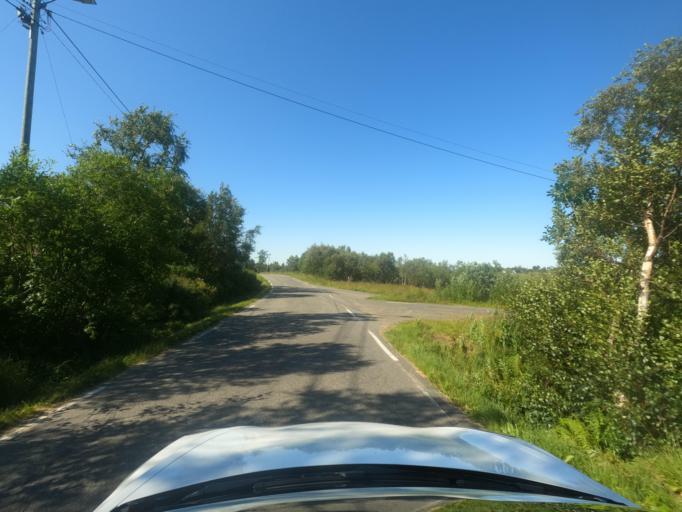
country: NO
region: Nordland
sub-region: Hadsel
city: Melbu
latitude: 68.4342
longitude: 14.7533
